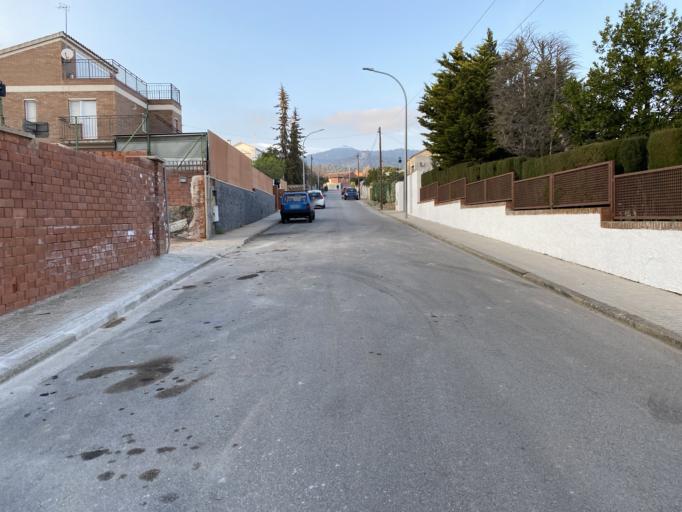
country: ES
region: Catalonia
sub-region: Provincia de Barcelona
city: Viladecavalls
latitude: 41.5587
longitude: 1.9522
